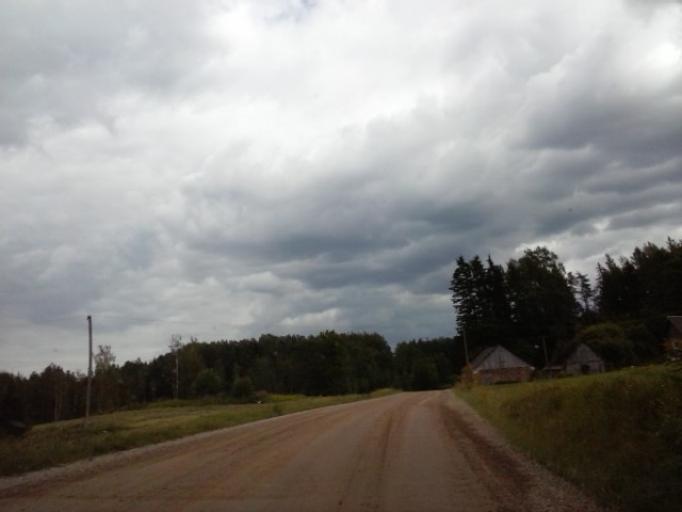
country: EE
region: Vorumaa
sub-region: Voru linn
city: Voru
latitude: 57.7491
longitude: 27.0612
